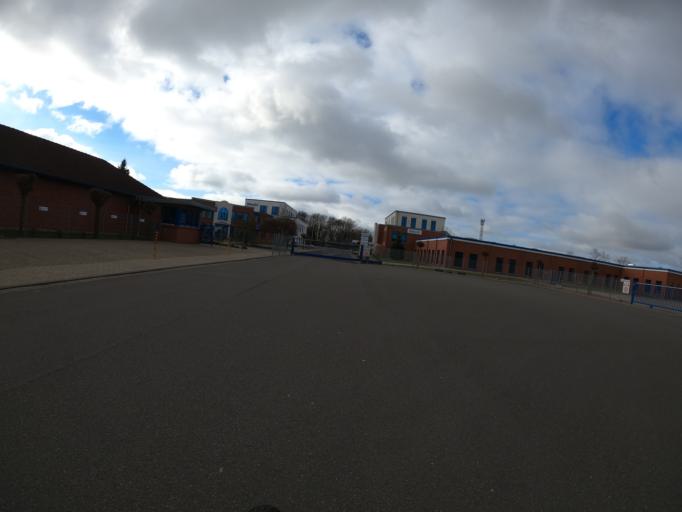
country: DE
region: Lower Saxony
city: Herzlake
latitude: 52.6833
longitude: 7.5920
